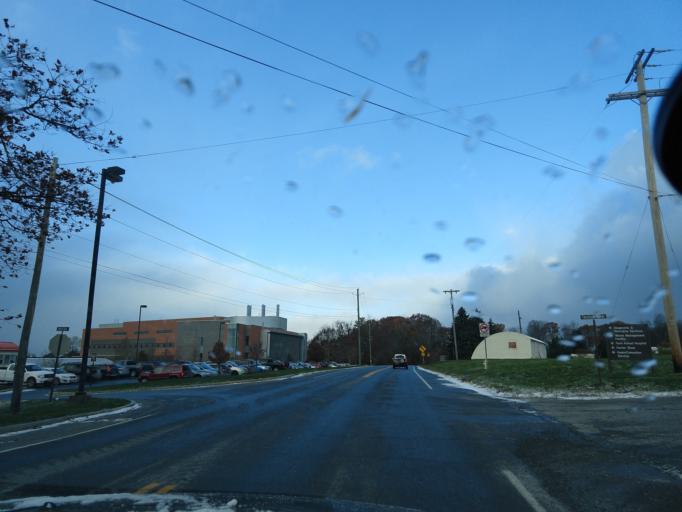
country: US
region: New York
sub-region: Tompkins County
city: East Ithaca
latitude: 42.4480
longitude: -76.4620
